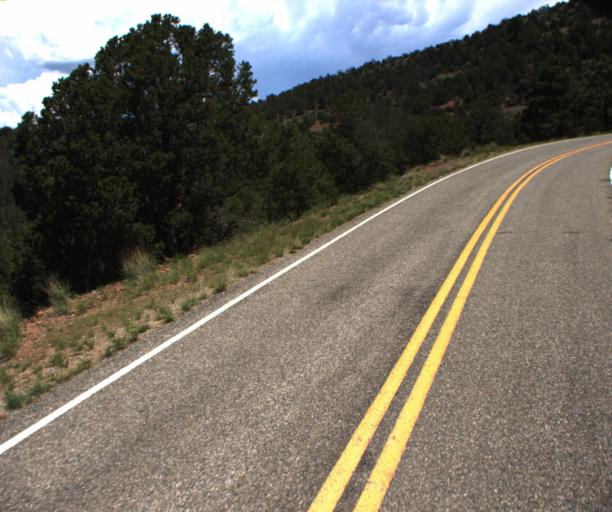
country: US
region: Arizona
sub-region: Greenlee County
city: Morenci
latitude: 33.3699
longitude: -109.3286
